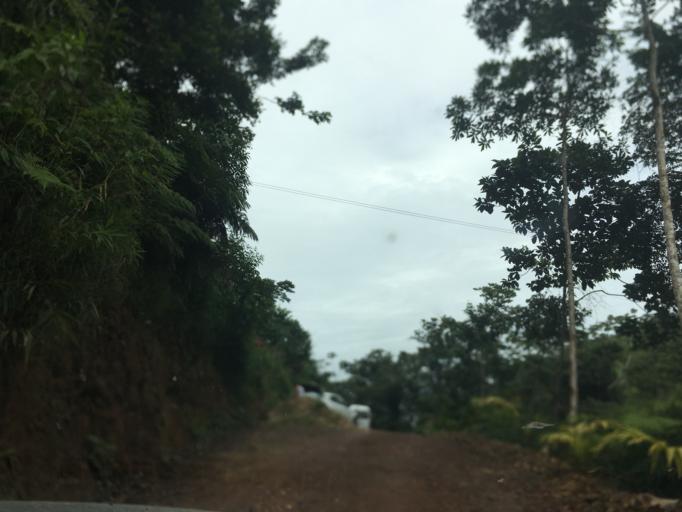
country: BZ
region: Stann Creek
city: Placencia
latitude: 16.7456
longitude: -88.4484
